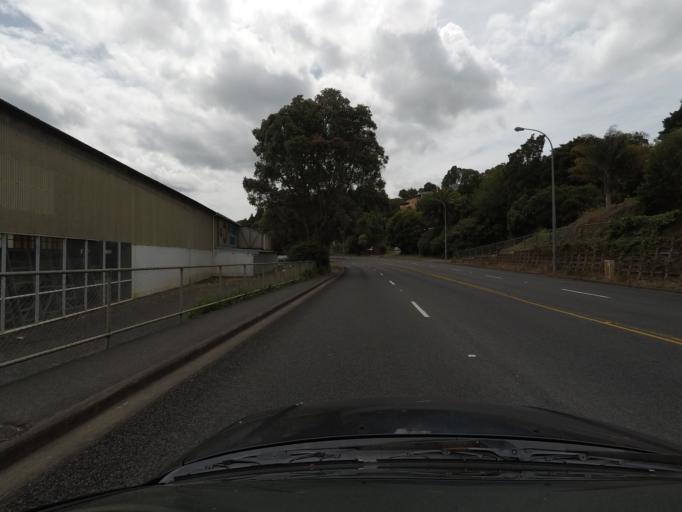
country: NZ
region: Northland
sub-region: Whangarei
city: Whangarei
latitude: -35.7258
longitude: 174.3317
